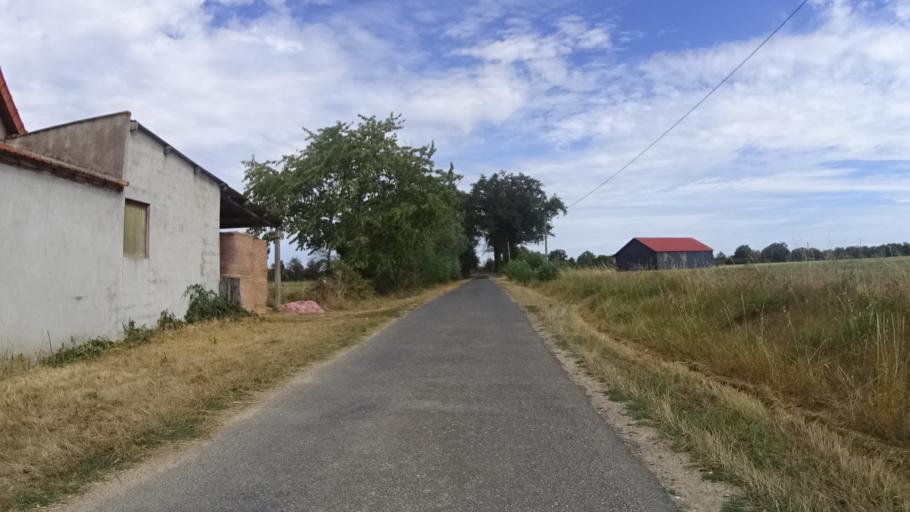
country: FR
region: Auvergne
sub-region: Departement de l'Allier
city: Beaulon
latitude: 46.6645
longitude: 3.6569
